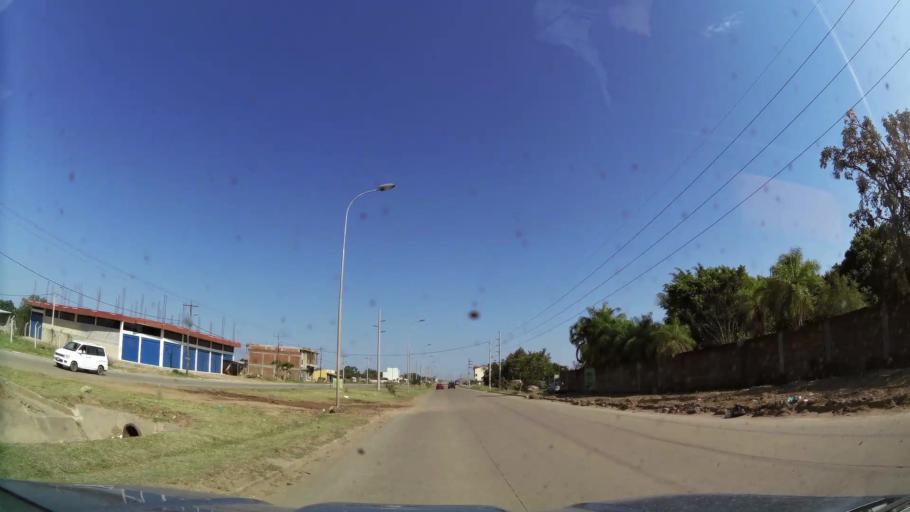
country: BO
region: Santa Cruz
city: Cotoca
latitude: -17.7845
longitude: -63.1079
